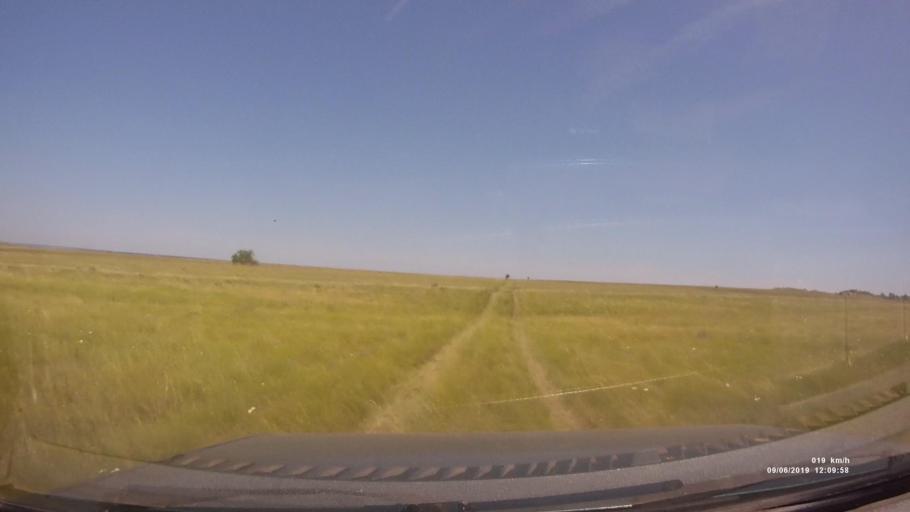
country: RU
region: Rostov
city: Staraya Stanitsa
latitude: 48.2491
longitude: 40.3383
